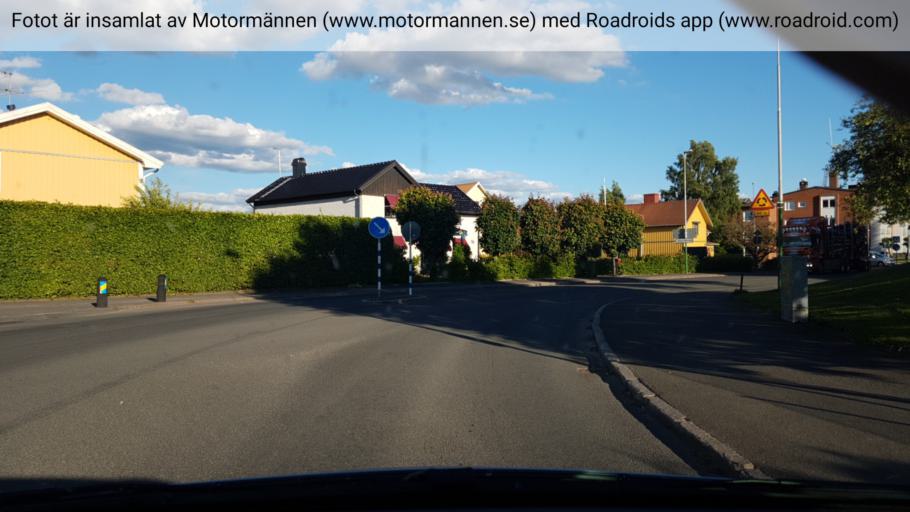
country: SE
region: Vaestra Goetaland
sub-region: Tidaholms Kommun
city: Tidaholm
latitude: 58.1856
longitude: 13.9595
